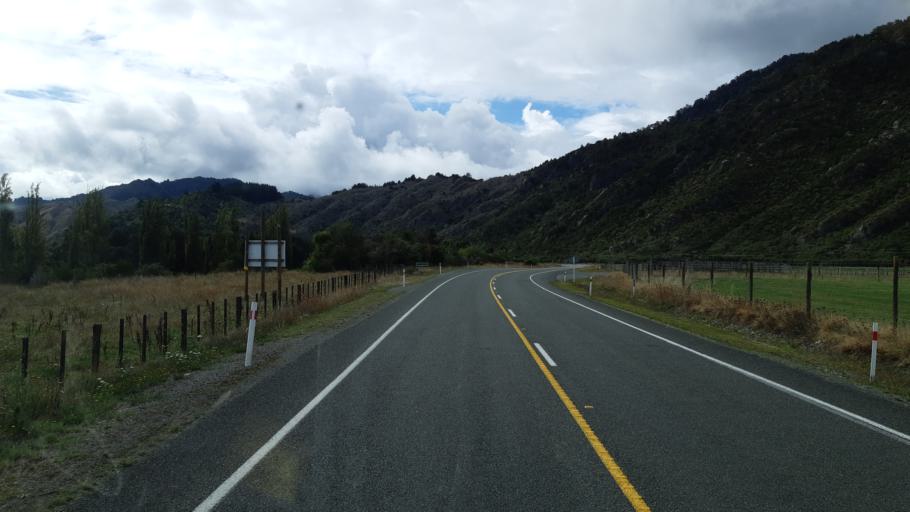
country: NZ
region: West Coast
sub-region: Buller District
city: Westport
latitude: -41.7965
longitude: 172.3533
